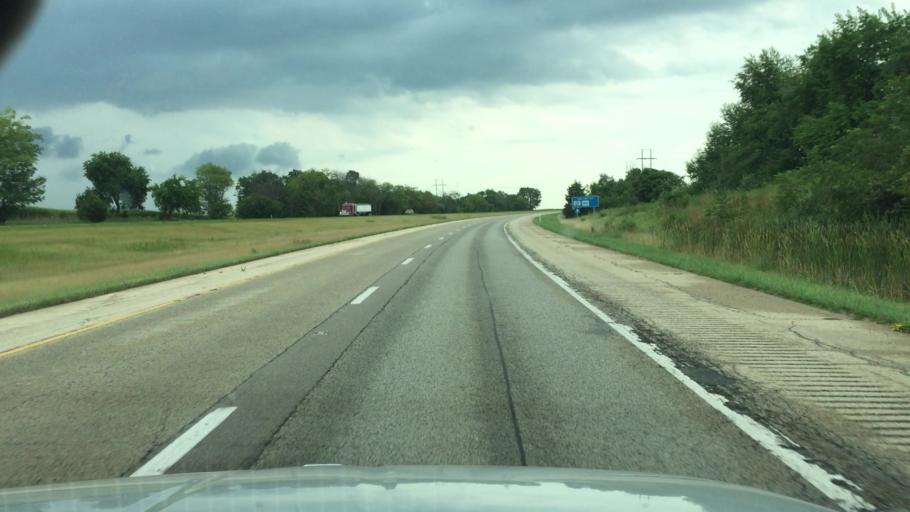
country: US
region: Illinois
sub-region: Peoria County
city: Hanna City
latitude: 40.7868
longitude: -89.7786
